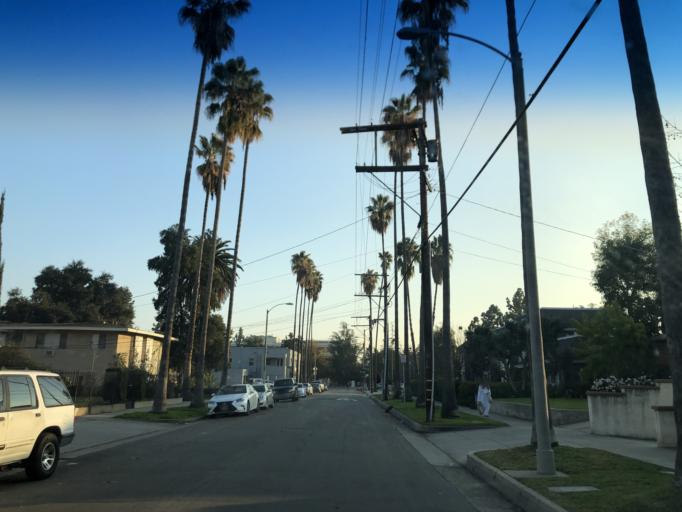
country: US
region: California
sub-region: Los Angeles County
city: Pasadena
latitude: 34.1472
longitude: -118.1199
